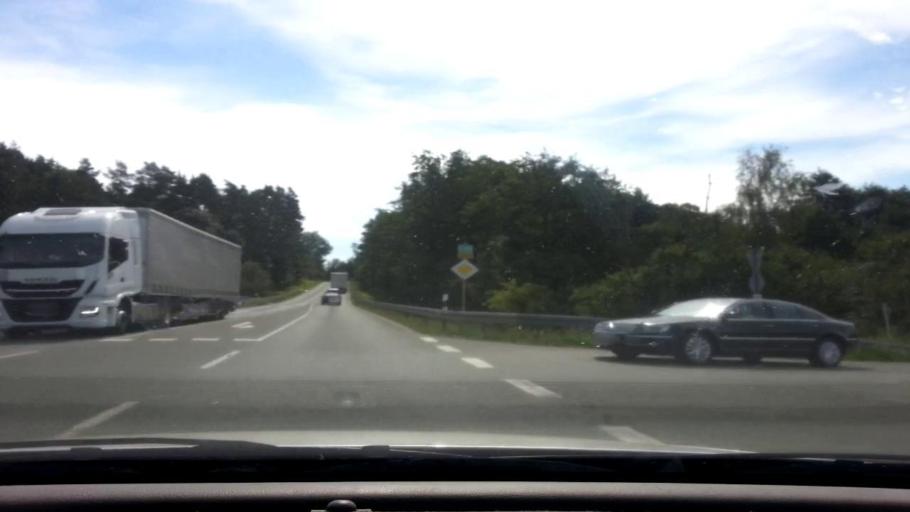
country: DE
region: Bavaria
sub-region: Upper Franconia
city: Gesees
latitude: 50.0471
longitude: 11.6438
